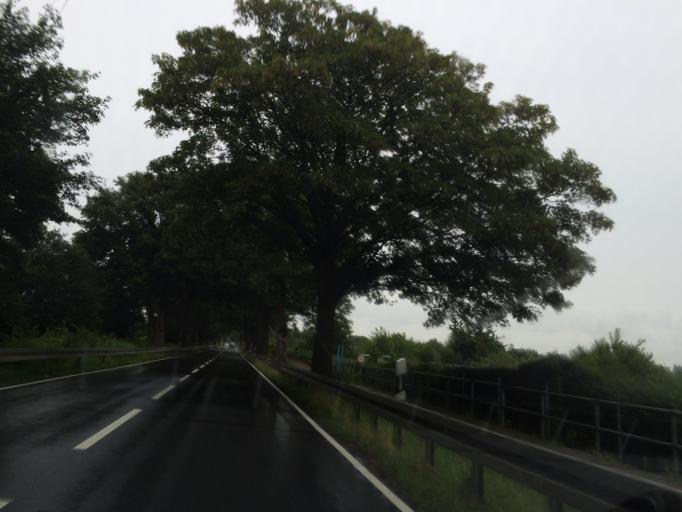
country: DE
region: Mecklenburg-Vorpommern
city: Kramerhof
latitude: 54.3373
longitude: 13.0582
